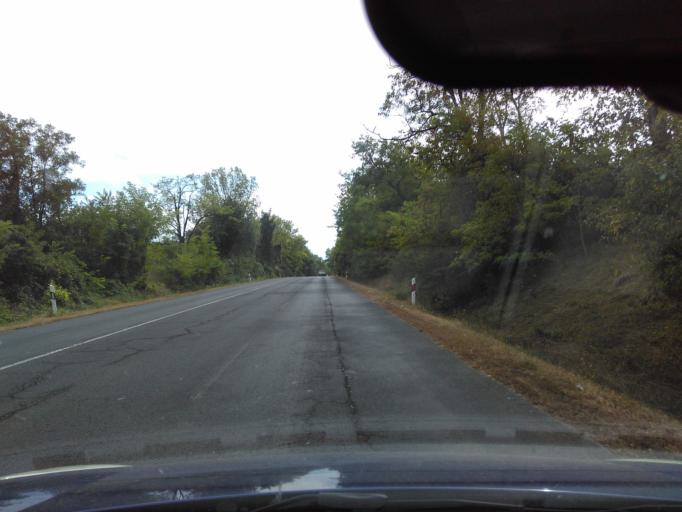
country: HU
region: Pest
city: Aszod
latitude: 47.6406
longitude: 19.4628
